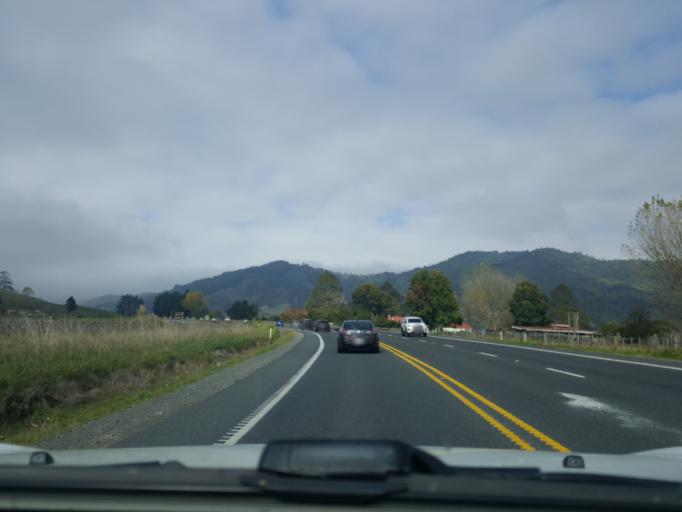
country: NZ
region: Waikato
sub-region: Waikato District
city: Ngaruawahia
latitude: -37.5918
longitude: 175.1594
